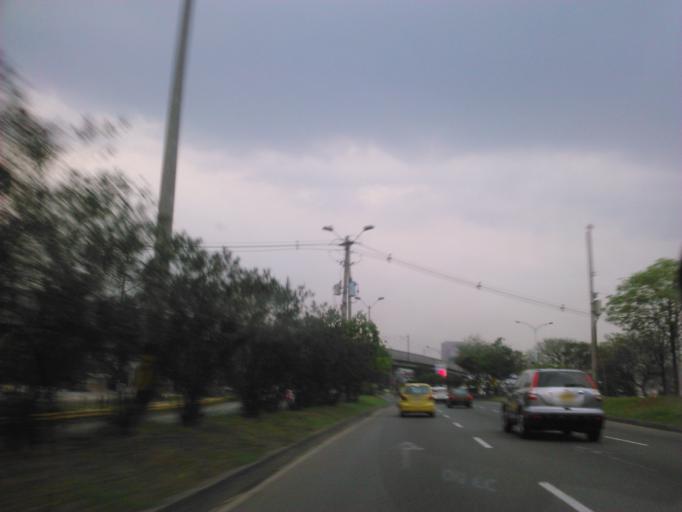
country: CO
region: Antioquia
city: Medellin
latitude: 6.2325
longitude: -75.5750
